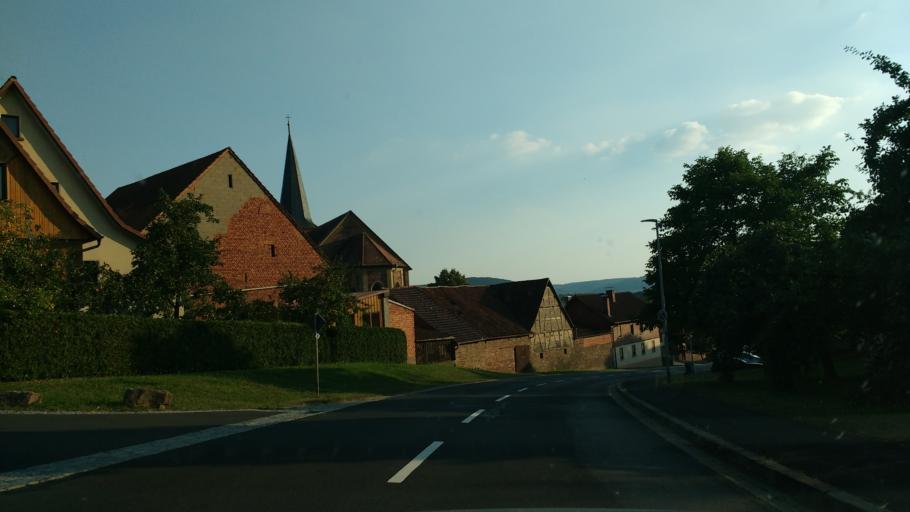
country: DE
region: Bavaria
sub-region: Regierungsbezirk Unterfranken
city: Elfershausen
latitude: 50.1489
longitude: 9.9609
